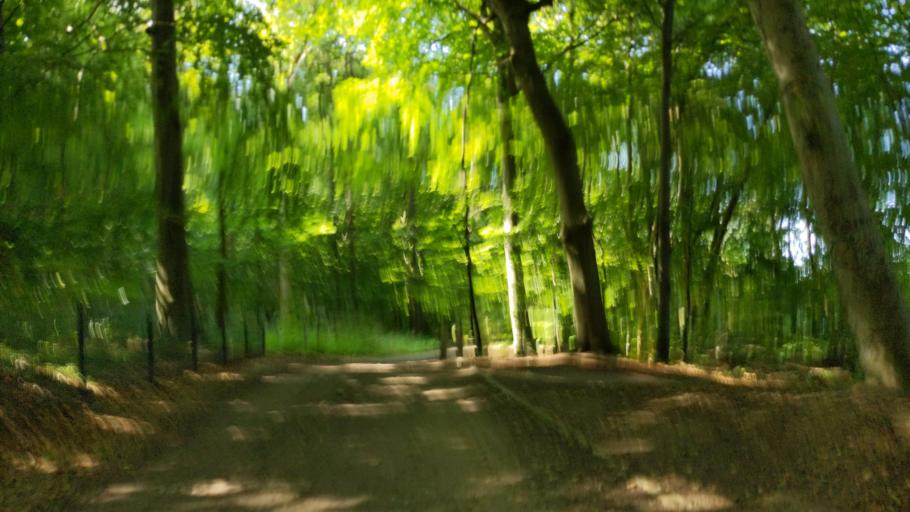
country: DE
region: Schleswig-Holstein
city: Malente
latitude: 54.1604
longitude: 10.5405
